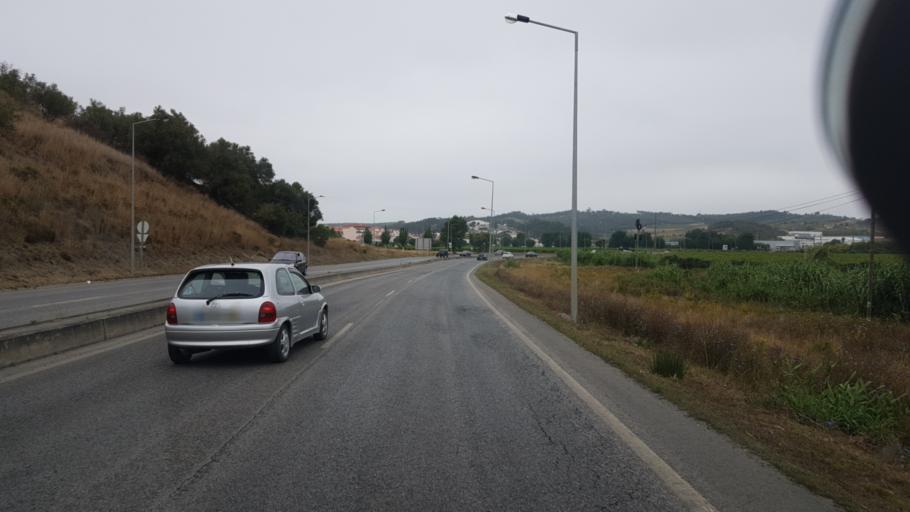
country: PT
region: Lisbon
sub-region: Torres Vedras
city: Torres Vedras
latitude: 39.0964
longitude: -9.2887
